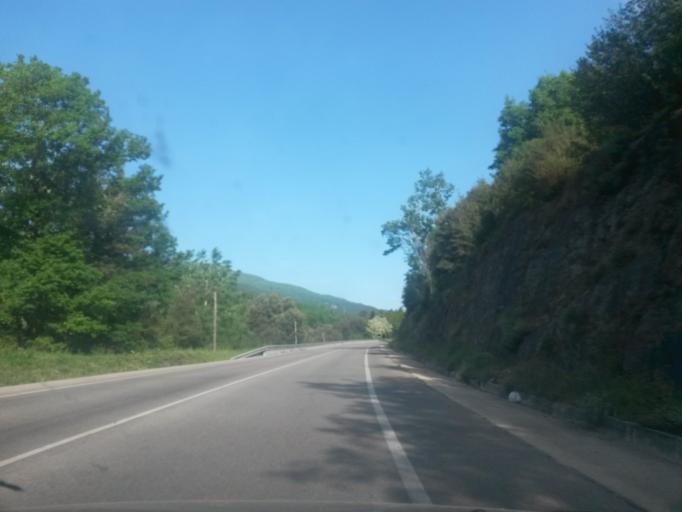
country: ES
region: Catalonia
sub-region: Provincia de Girona
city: les Planes d'Hostoles
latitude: 42.0459
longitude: 2.5530
